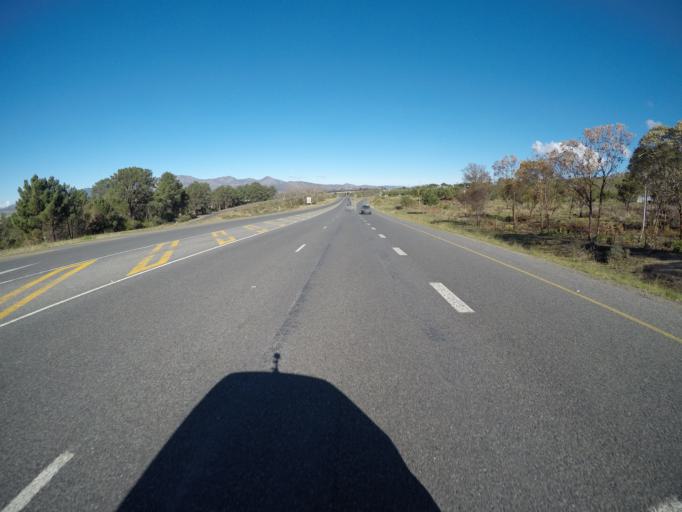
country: ZA
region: Western Cape
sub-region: Overberg District Municipality
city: Grabouw
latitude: -34.2260
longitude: 19.1877
